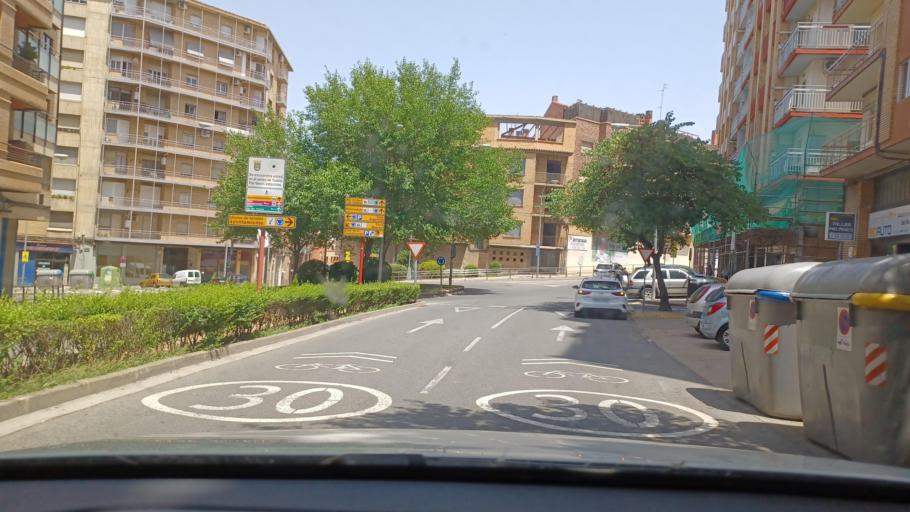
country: ES
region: Navarre
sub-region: Provincia de Navarra
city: Tudela
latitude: 42.0591
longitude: -1.6078
